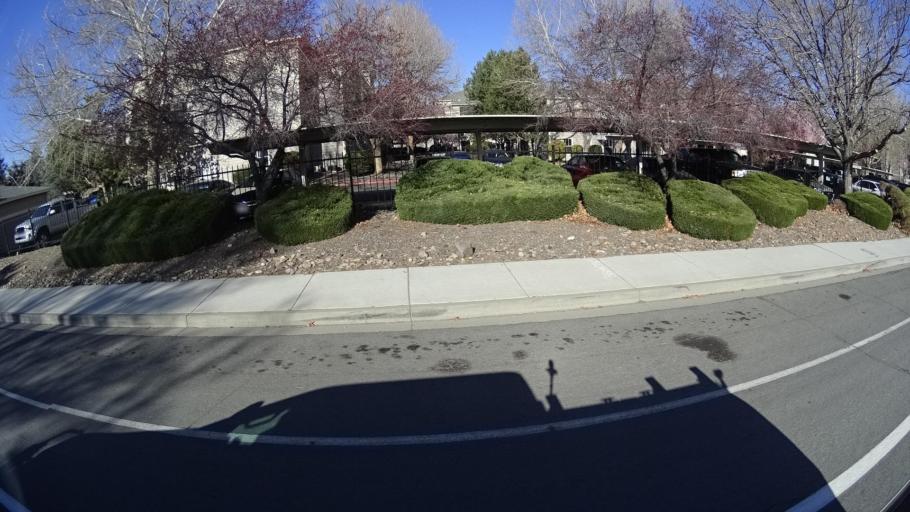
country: US
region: Nevada
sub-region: Washoe County
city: Sparks
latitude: 39.4488
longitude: -119.7712
